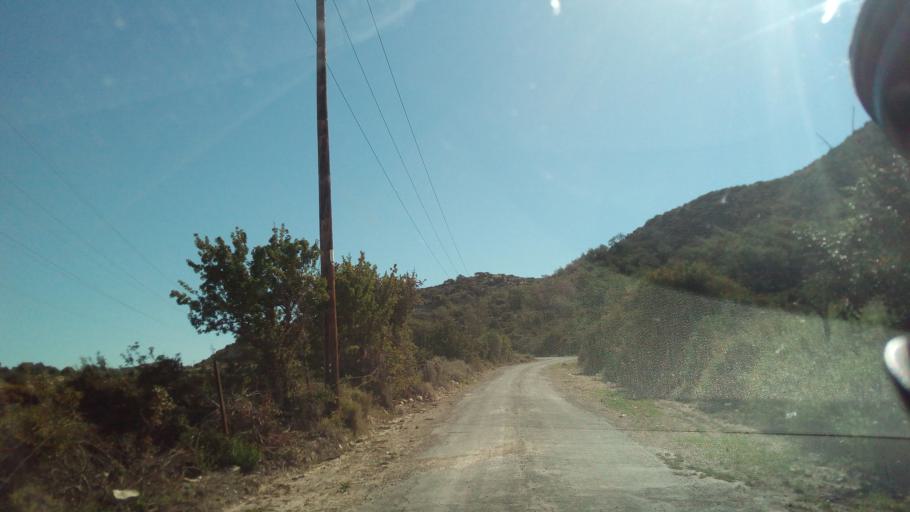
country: CY
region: Limassol
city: Pissouri
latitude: 34.6725
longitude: 32.6656
